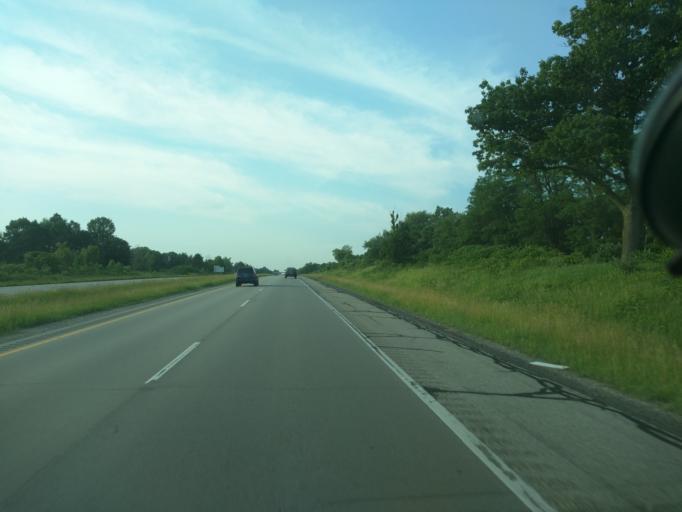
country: US
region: Michigan
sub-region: Ingham County
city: Leslie
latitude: 42.4677
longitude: -84.4435
